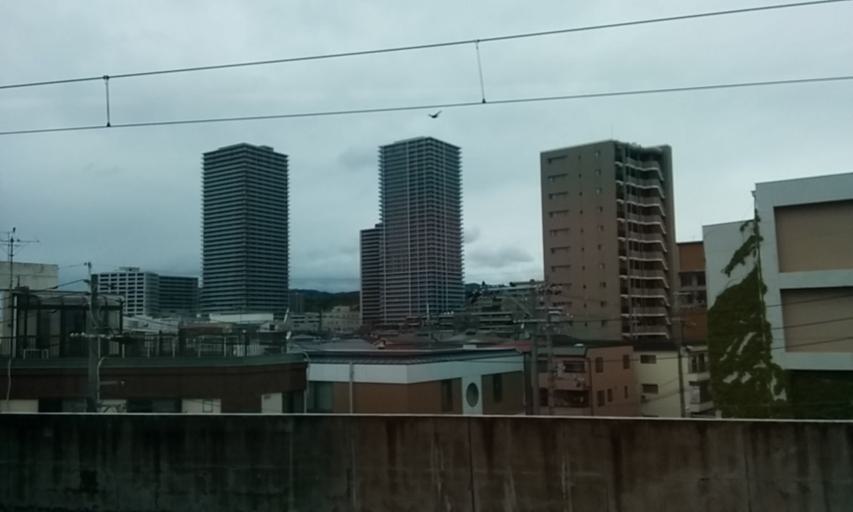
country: JP
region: Osaka
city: Takatsuki
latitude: 34.8703
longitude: 135.6521
